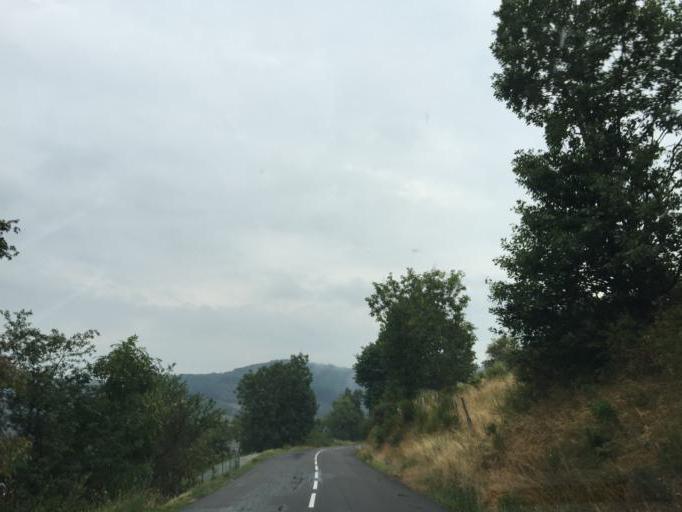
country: FR
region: Rhone-Alpes
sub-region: Departement de la Loire
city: Saint-Christo-en-Jarez
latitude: 45.5311
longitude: 4.4916
